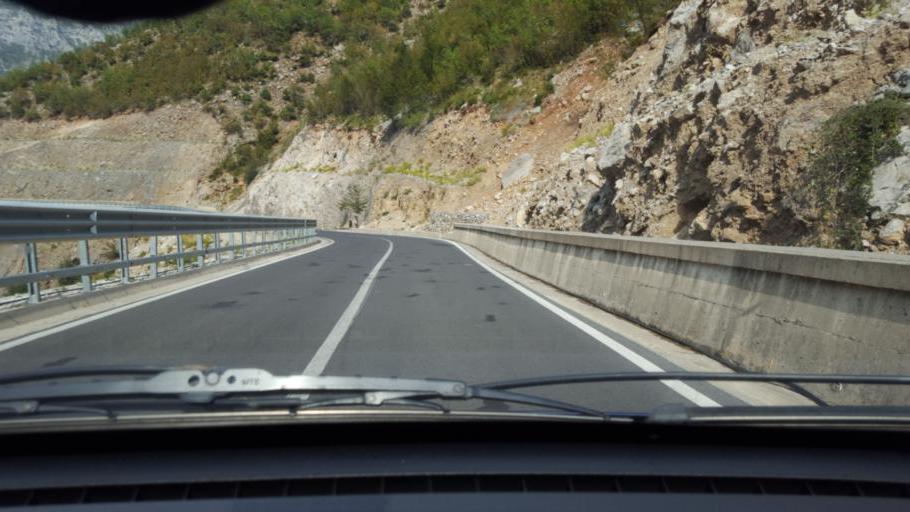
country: AL
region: Shkoder
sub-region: Rrethi i Malesia e Madhe
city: Kastrat
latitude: 42.4141
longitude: 19.5108
